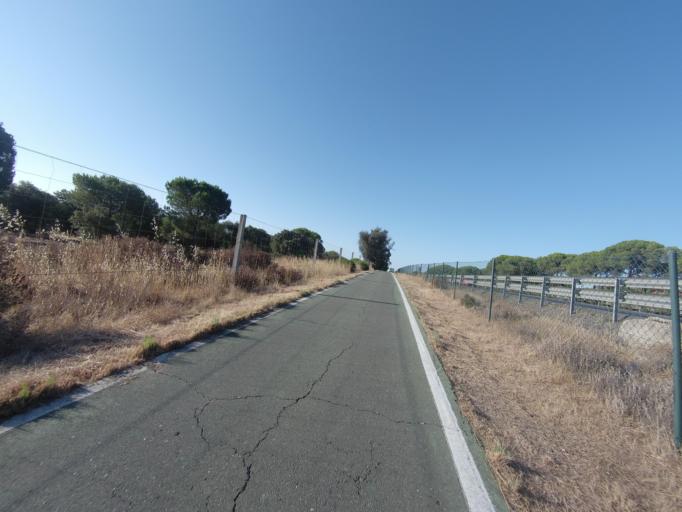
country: ES
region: Andalusia
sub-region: Provincia de Huelva
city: Aljaraque
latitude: 37.2432
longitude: -7.0183
